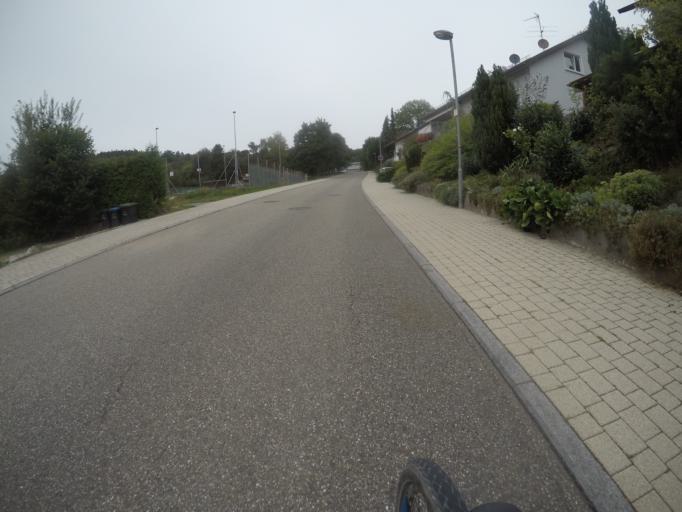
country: DE
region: Baden-Wuerttemberg
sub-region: Karlsruhe Region
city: Simmozheim
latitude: 48.7770
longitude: 8.8131
